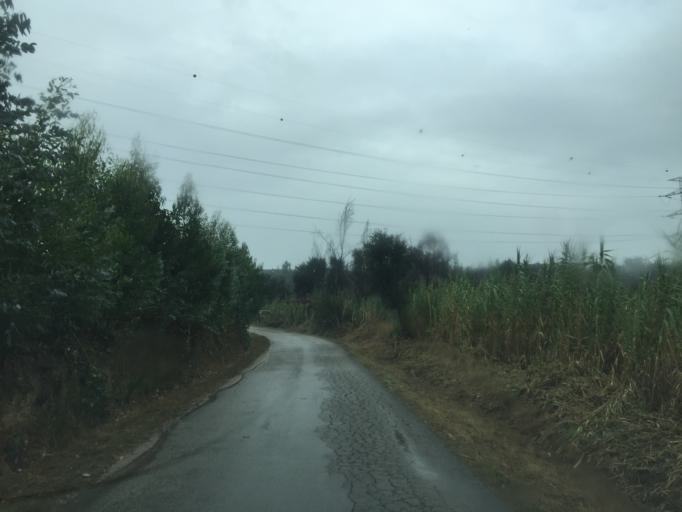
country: PT
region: Coimbra
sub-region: Figueira da Foz
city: Lavos
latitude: 40.0820
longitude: -8.8000
